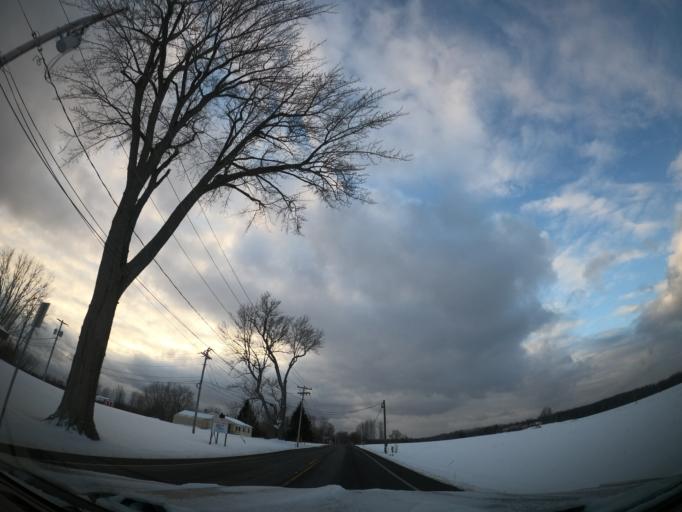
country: US
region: New York
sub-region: Onondaga County
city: Brewerton
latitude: 43.2014
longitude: -76.1738
